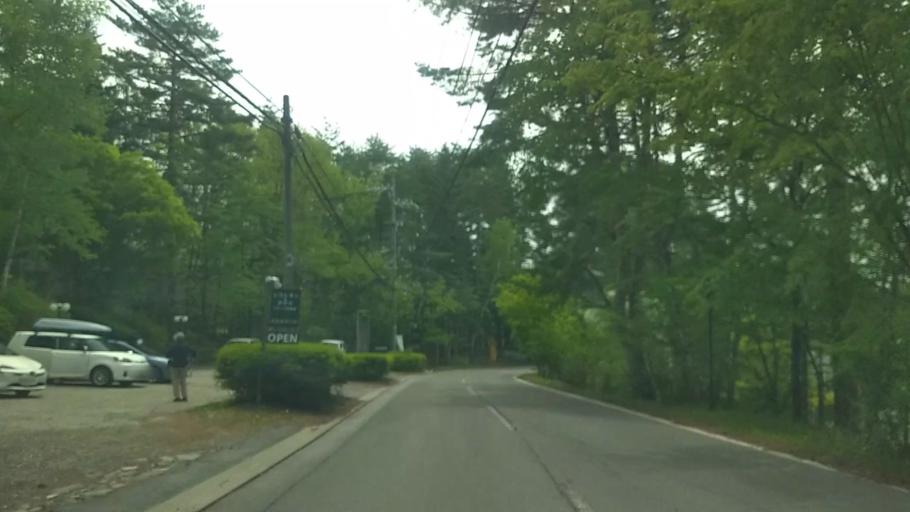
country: JP
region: Nagano
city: Chino
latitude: 36.0455
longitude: 138.2692
